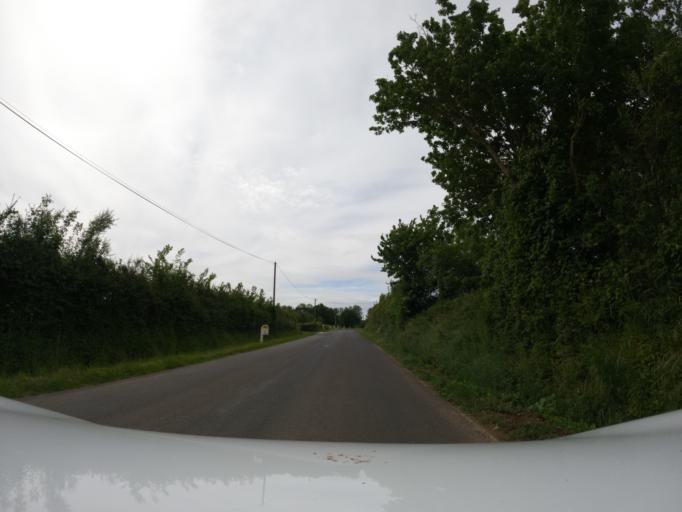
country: FR
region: Pays de la Loire
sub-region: Departement de la Vendee
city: Foussais-Payre
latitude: 46.5133
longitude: -0.6497
